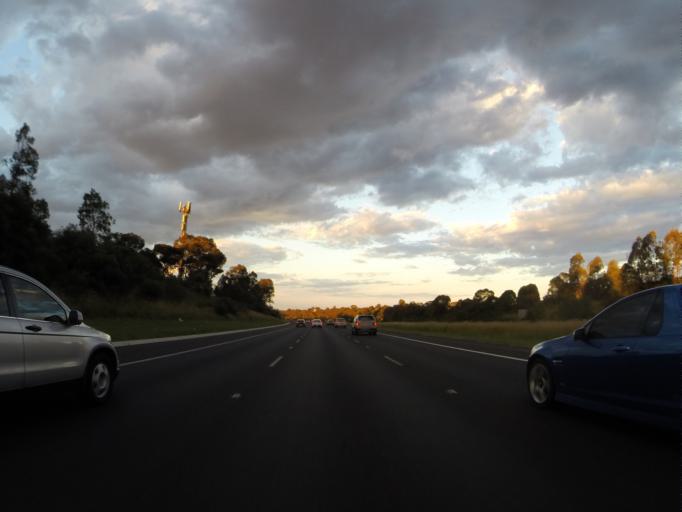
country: AU
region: New South Wales
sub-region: Campbelltown Municipality
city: Campbelltown
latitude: -34.0520
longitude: 150.8106
